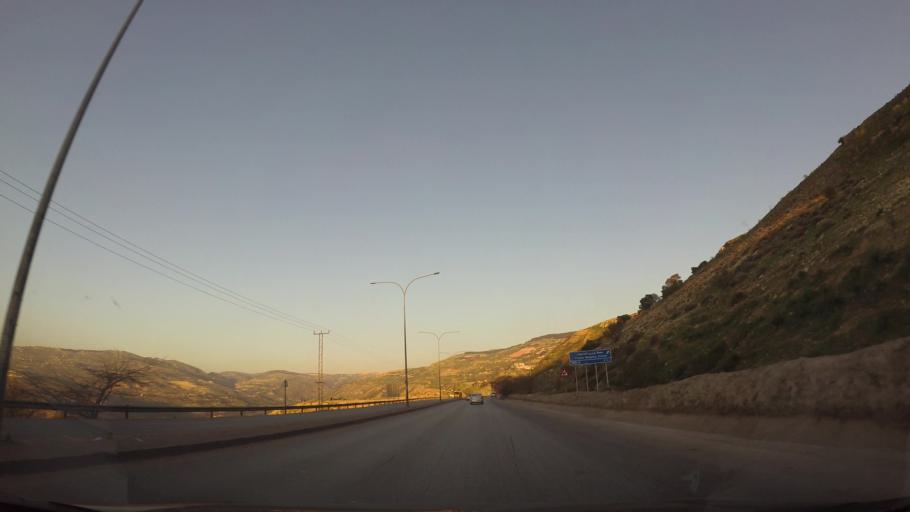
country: JO
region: Amman
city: Wadi as Sir
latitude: 31.8685
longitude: 35.7398
